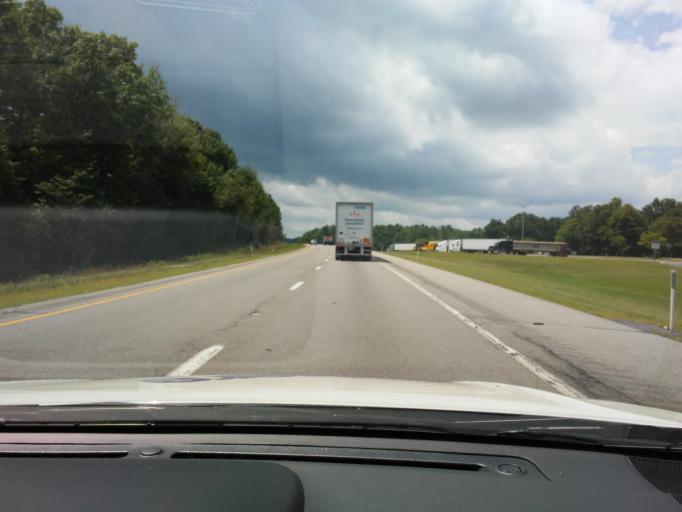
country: US
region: Pennsylvania
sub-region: Centre County
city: Milesburg
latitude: 41.0205
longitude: -77.9509
